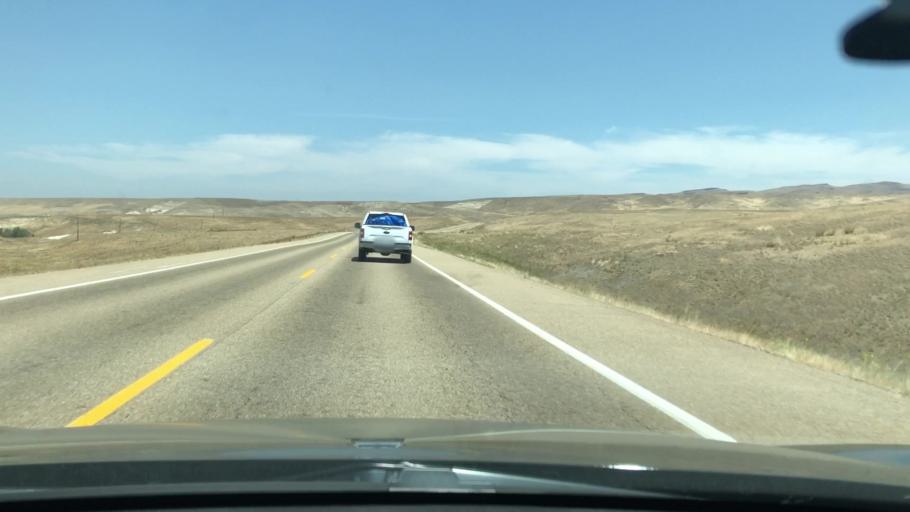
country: US
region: Idaho
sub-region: Owyhee County
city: Marsing
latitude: 43.2696
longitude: -117.0033
